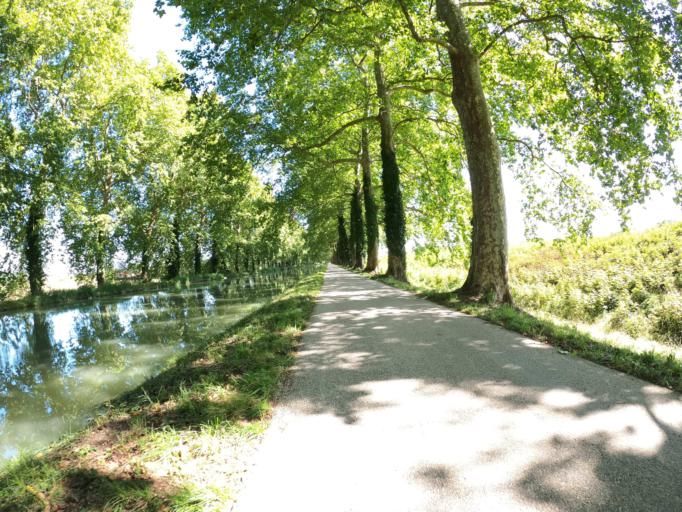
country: FR
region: Midi-Pyrenees
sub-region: Departement du Tarn-et-Garonne
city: Auvillar
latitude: 44.0951
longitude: 0.9432
